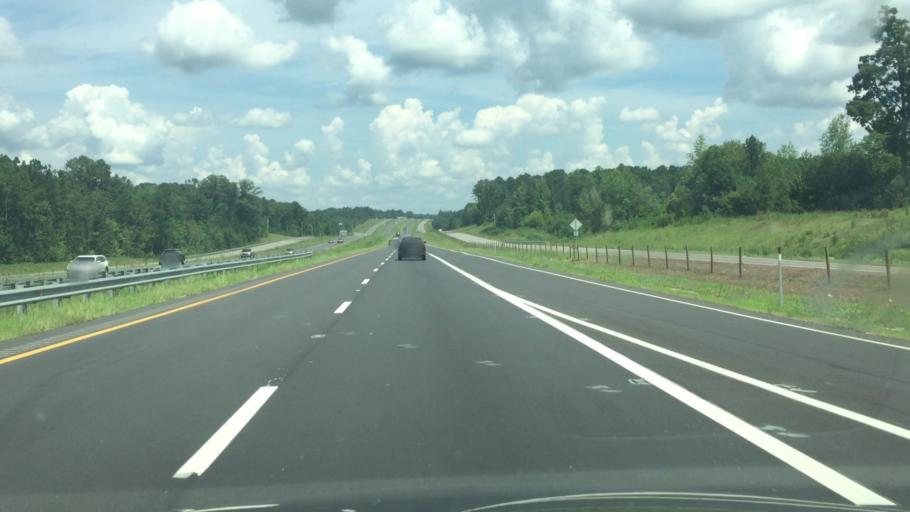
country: US
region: North Carolina
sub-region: Richmond County
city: Ellerbe
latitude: 35.0171
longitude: -79.7700
